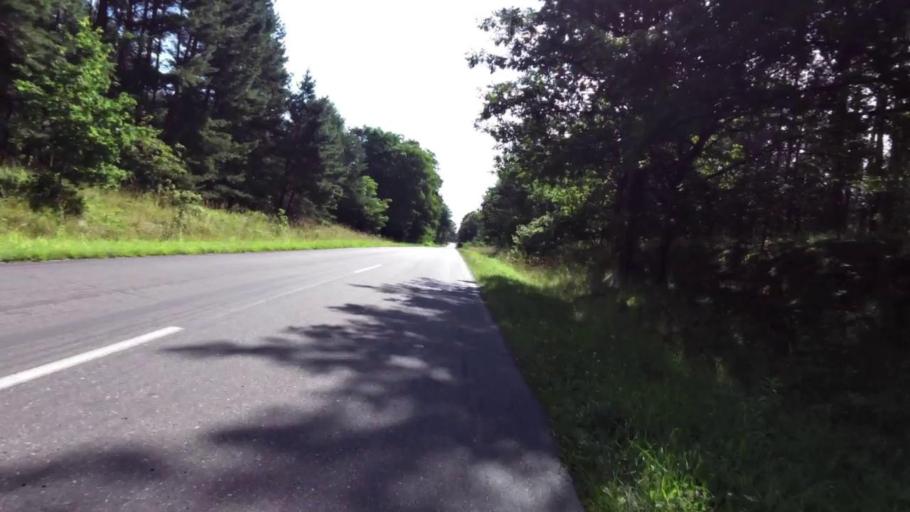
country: PL
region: West Pomeranian Voivodeship
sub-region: Powiat stargardzki
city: Dobrzany
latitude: 53.3678
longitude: 15.3931
